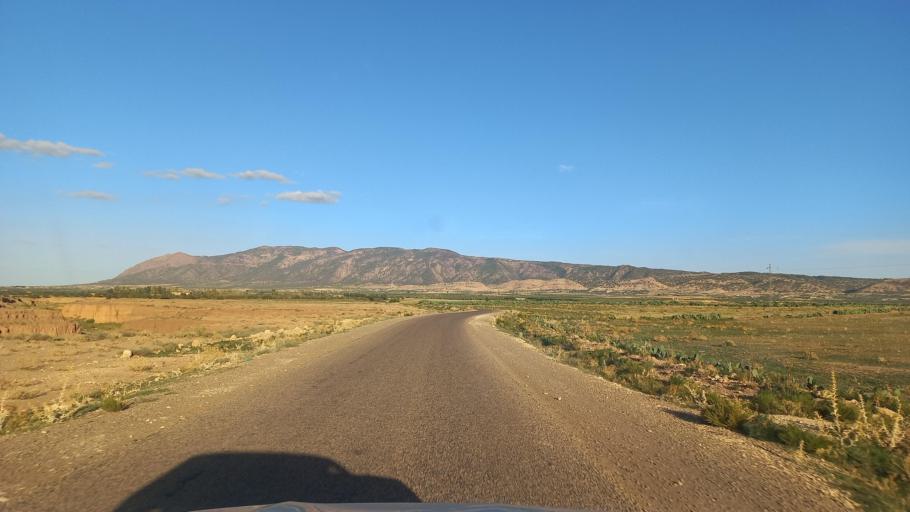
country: TN
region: Al Qasrayn
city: Sbiba
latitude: 35.4111
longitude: 9.1385
